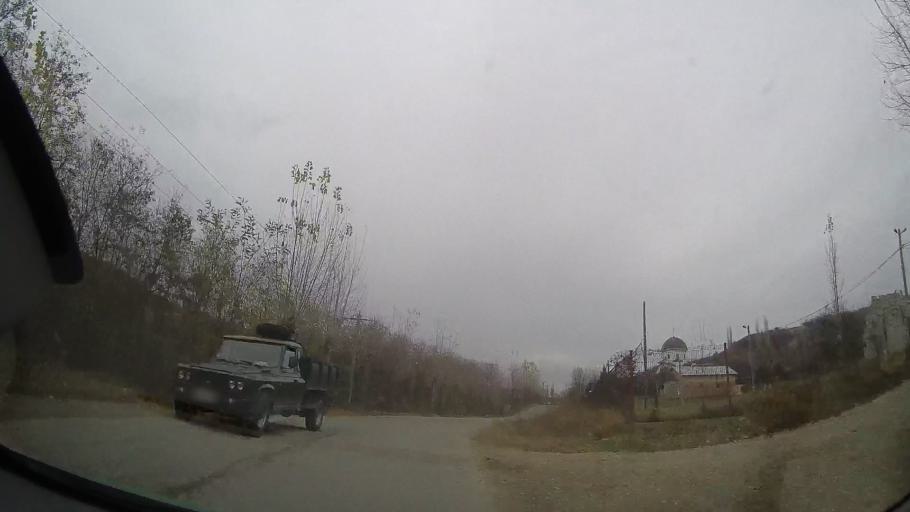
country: RO
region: Prahova
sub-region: Comuna Gornet-Cricov
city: Gornet-Cricov
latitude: 45.0529
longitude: 26.2951
